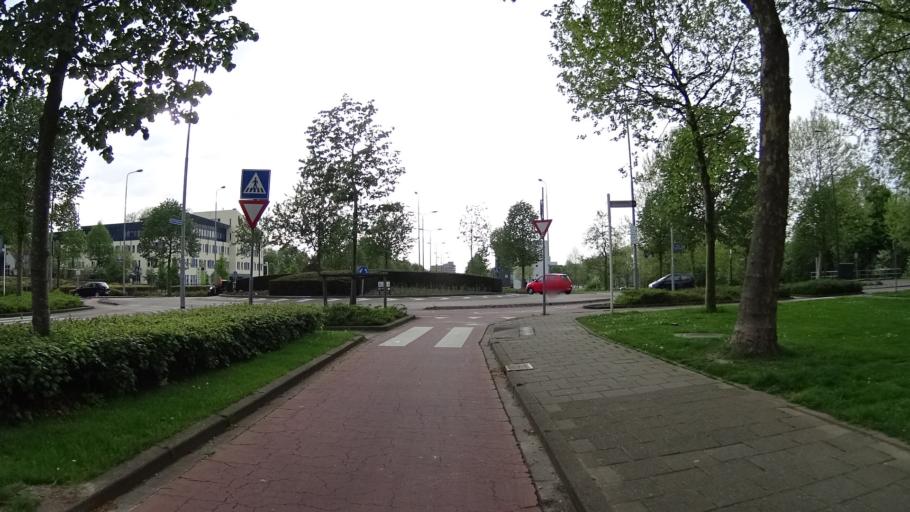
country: NL
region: North Brabant
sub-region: Gemeente 's-Hertogenbosch
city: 's-Hertogenbosch
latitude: 51.6917
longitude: 5.2802
